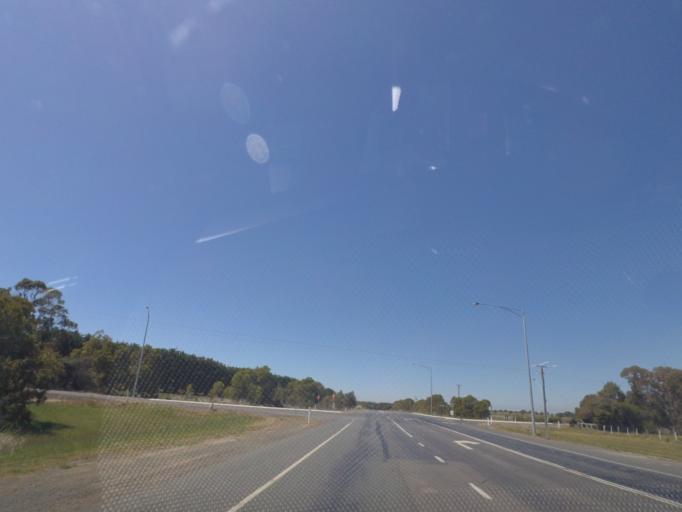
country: AU
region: Victoria
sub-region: Hume
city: Sunbury
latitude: -37.4255
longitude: 144.7279
